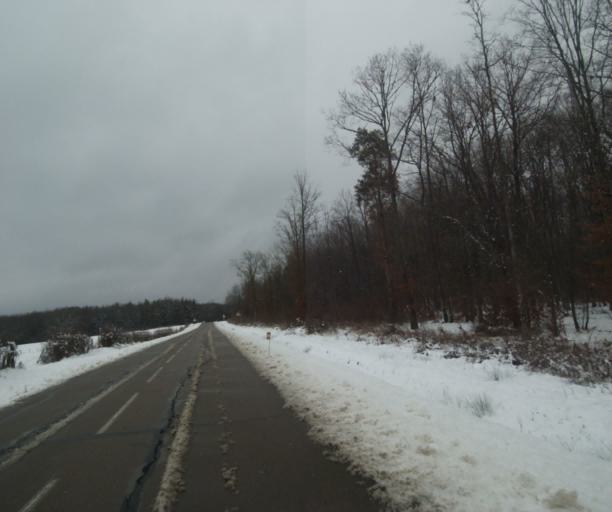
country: FR
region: Champagne-Ardenne
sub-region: Departement de la Haute-Marne
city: Laneuville-a-Remy
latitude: 48.4379
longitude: 4.8570
